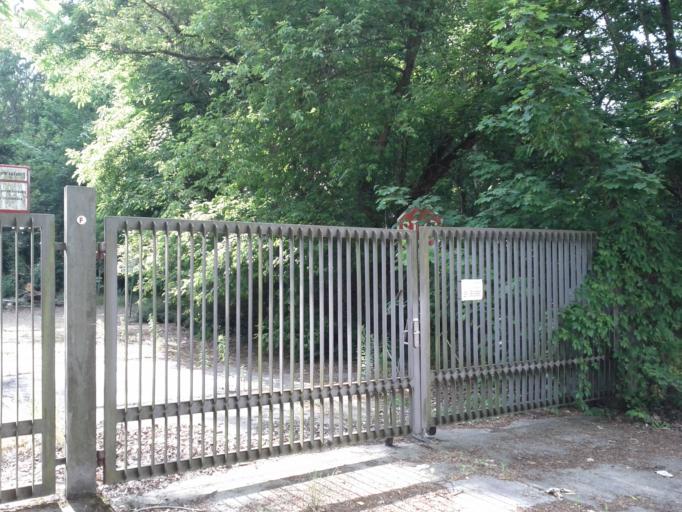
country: DE
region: Berlin
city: Friedrichshagen
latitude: 52.4538
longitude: 13.6169
